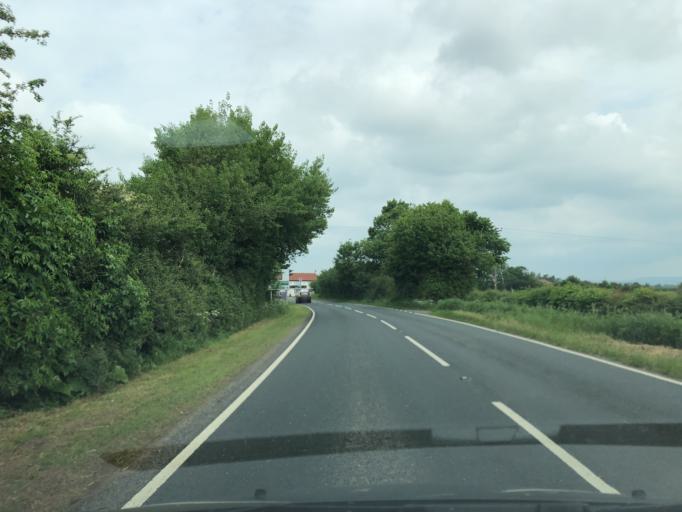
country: GB
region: England
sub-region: North Yorkshire
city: Thirsk
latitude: 54.2201
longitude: -1.4147
